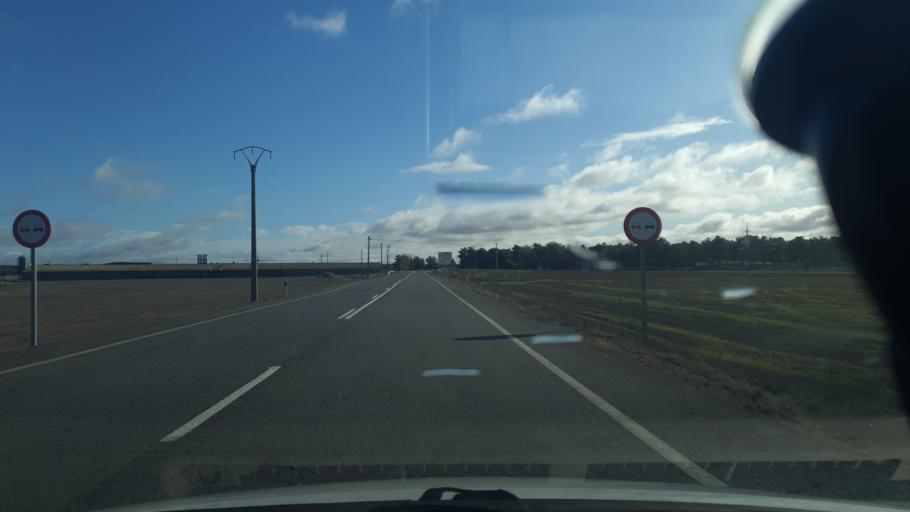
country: ES
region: Castille and Leon
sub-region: Provincia de Segovia
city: Martin Munoz de la Dehesa
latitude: 41.0469
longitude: -4.6872
